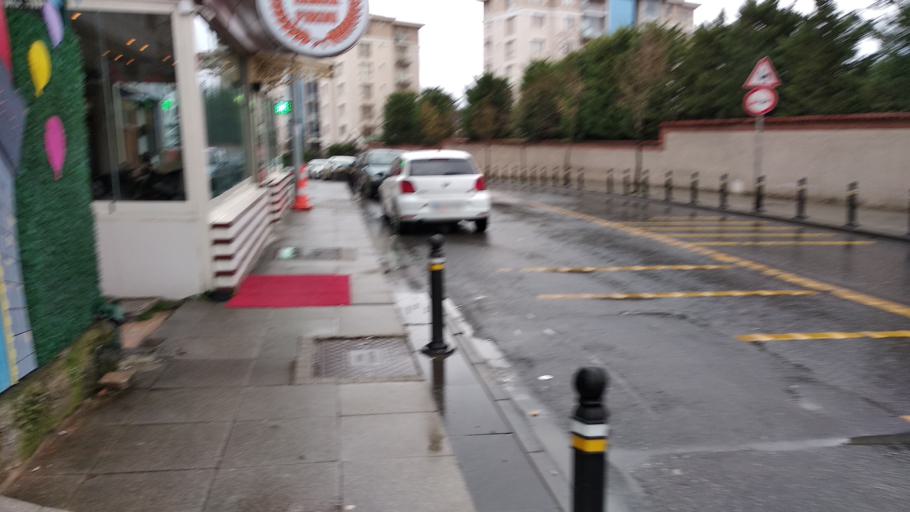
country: TR
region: Istanbul
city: Samandira
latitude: 41.0238
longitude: 29.1840
